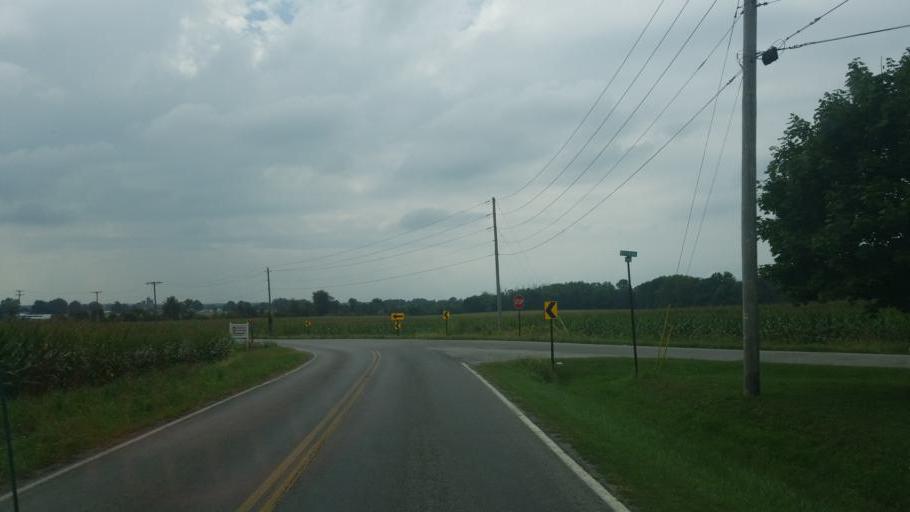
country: US
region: Ohio
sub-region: Wayne County
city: Rittman
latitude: 40.9659
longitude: -81.8281
